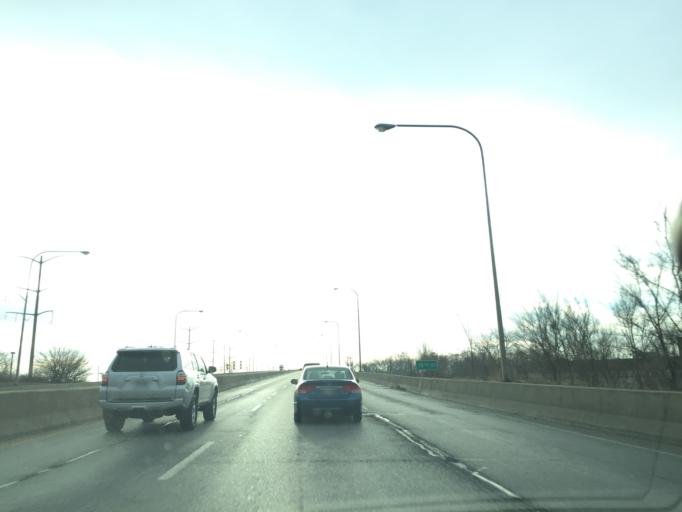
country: US
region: Illinois
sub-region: Cook County
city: Chicago
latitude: 41.7592
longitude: -87.5991
